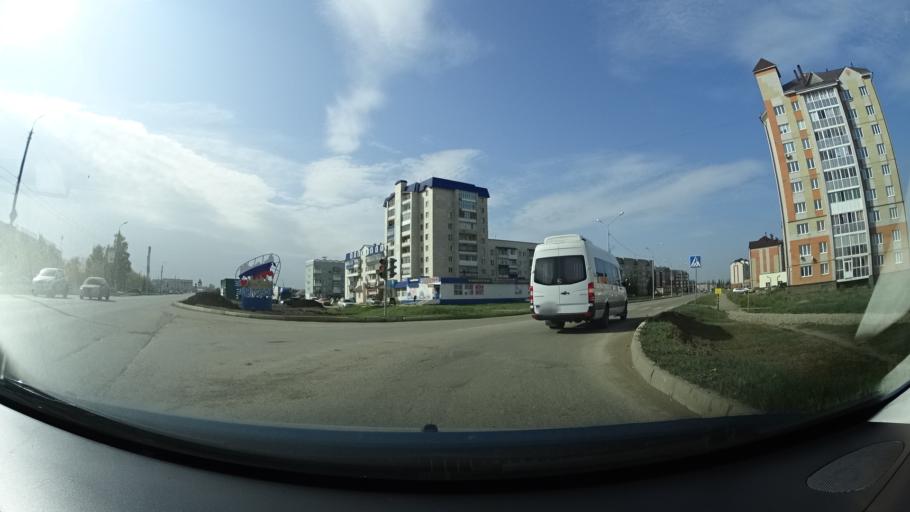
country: RU
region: Bashkortostan
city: Tuymazy
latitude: 54.5959
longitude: 53.7164
